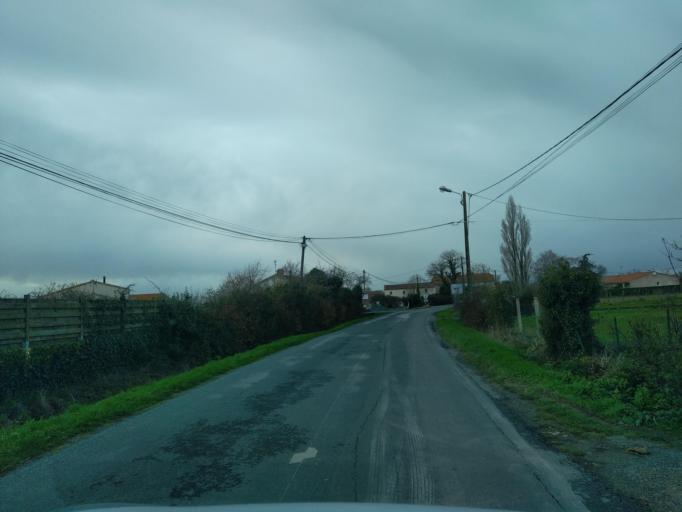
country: FR
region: Pays de la Loire
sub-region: Departement de la Vendee
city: Vix
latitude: 46.3518
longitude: -0.8395
